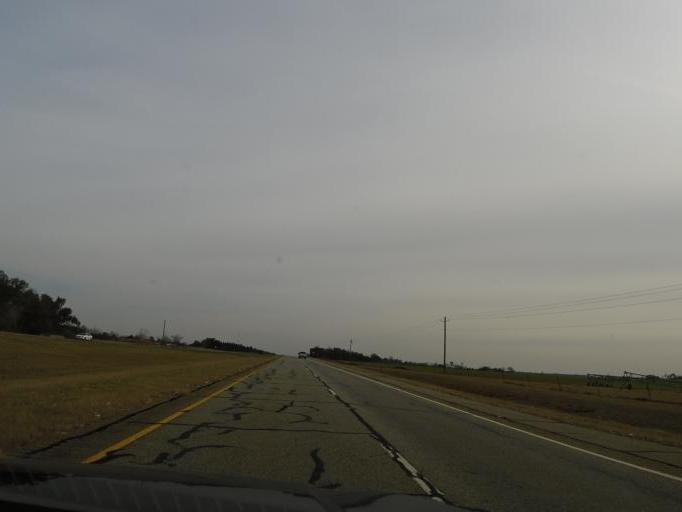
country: US
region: Georgia
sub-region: Seminole County
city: Donalsonville
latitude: 31.0619
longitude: -84.9289
